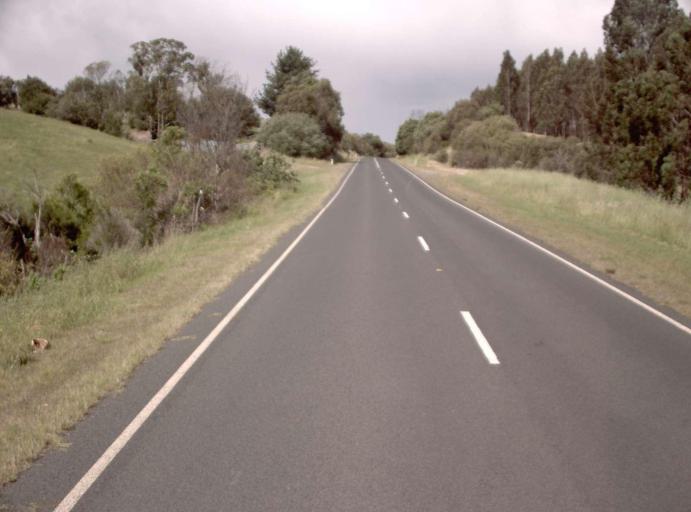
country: AU
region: Victoria
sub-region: Latrobe
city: Morwell
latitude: -38.1589
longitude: 146.4186
